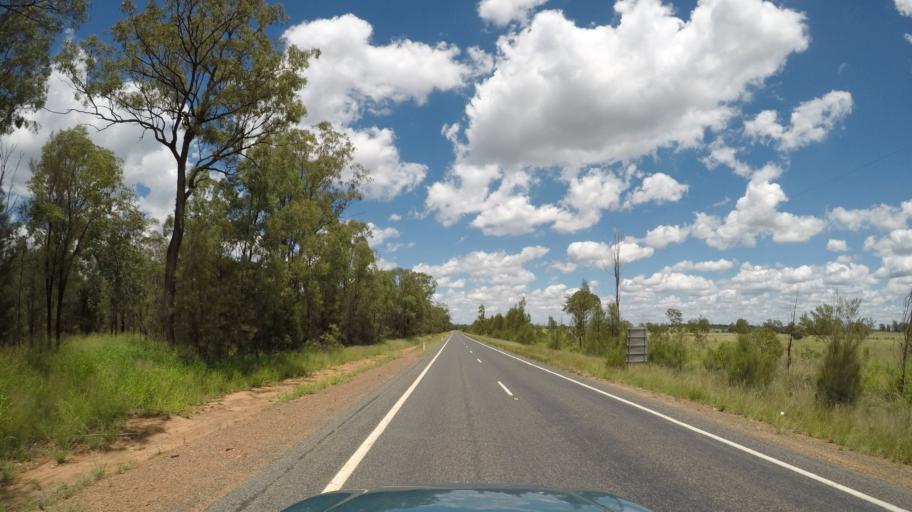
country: AU
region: Queensland
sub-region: Goondiwindi
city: Goondiwindi
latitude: -28.0027
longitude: 150.9343
